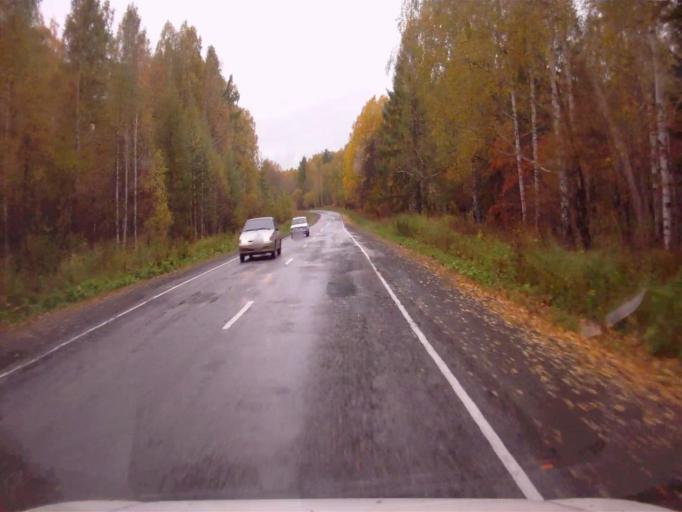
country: RU
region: Chelyabinsk
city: Nizhniy Ufaley
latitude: 56.0531
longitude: 59.9531
